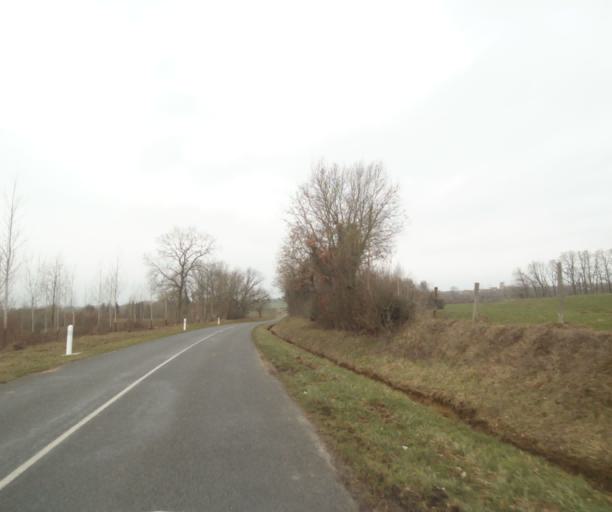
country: FR
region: Champagne-Ardenne
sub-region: Departement de la Marne
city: Pargny-sur-Saulx
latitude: 48.7398
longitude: 4.8537
